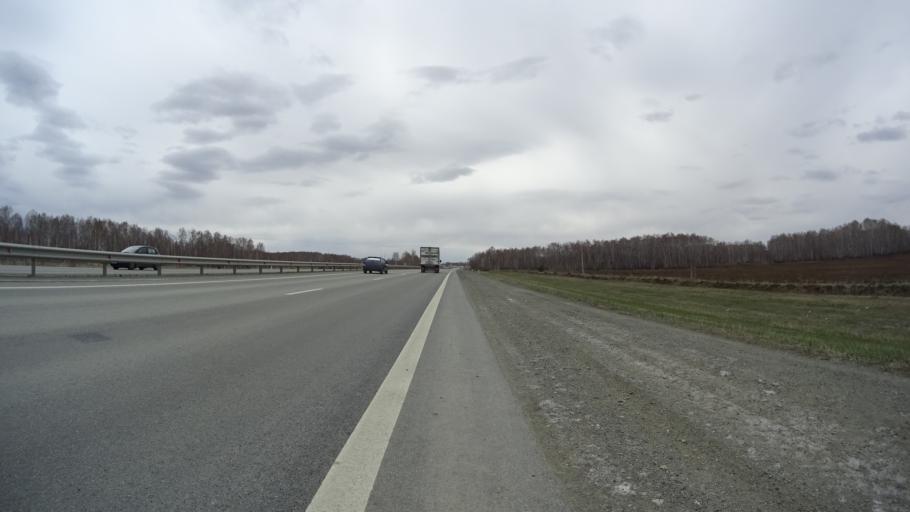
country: RU
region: Chelyabinsk
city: Yemanzhelinka
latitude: 54.8309
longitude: 61.3116
